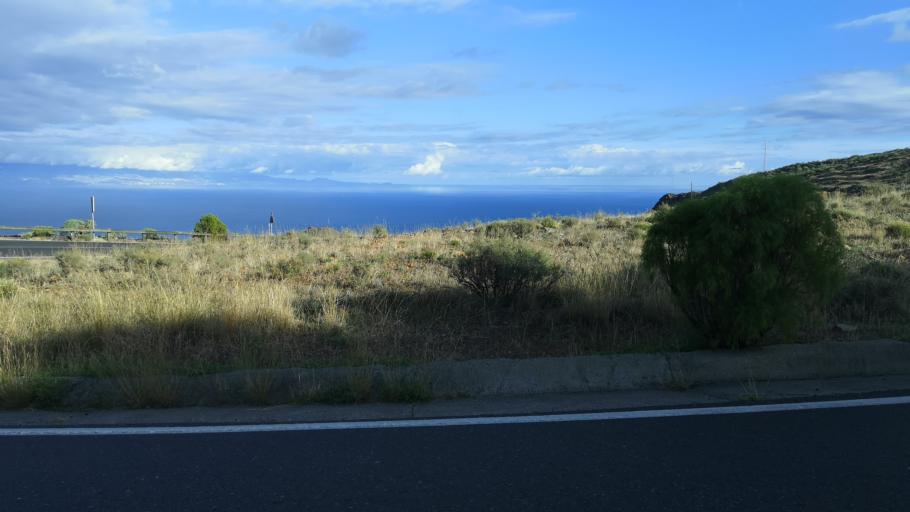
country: ES
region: Canary Islands
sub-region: Provincia de Santa Cruz de Tenerife
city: San Sebastian de la Gomera
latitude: 28.0859
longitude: -17.1378
